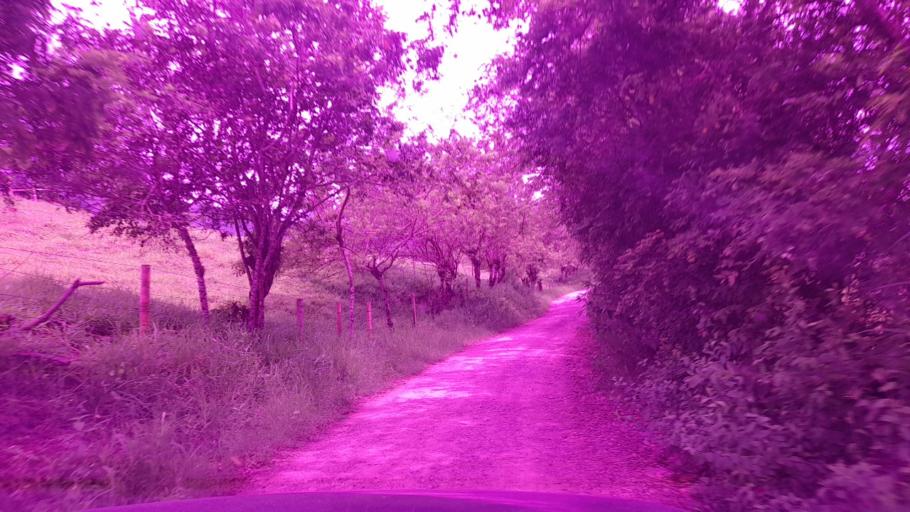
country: CO
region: Valle del Cauca
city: Andalucia
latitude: 4.1673
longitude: -76.0920
